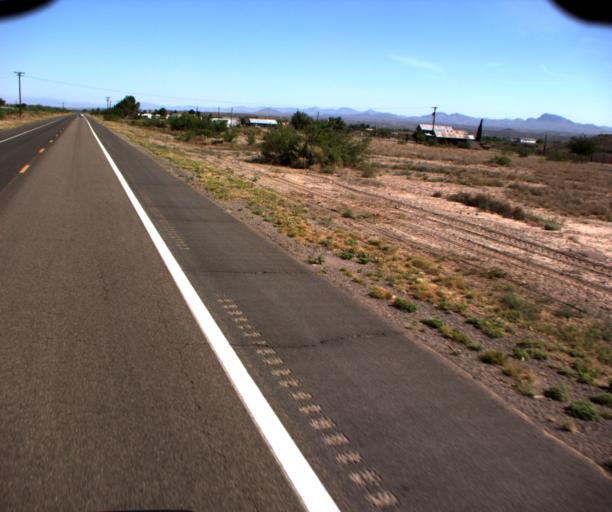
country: US
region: Arizona
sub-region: Greenlee County
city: Clifton
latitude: 32.6707
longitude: -109.0762
